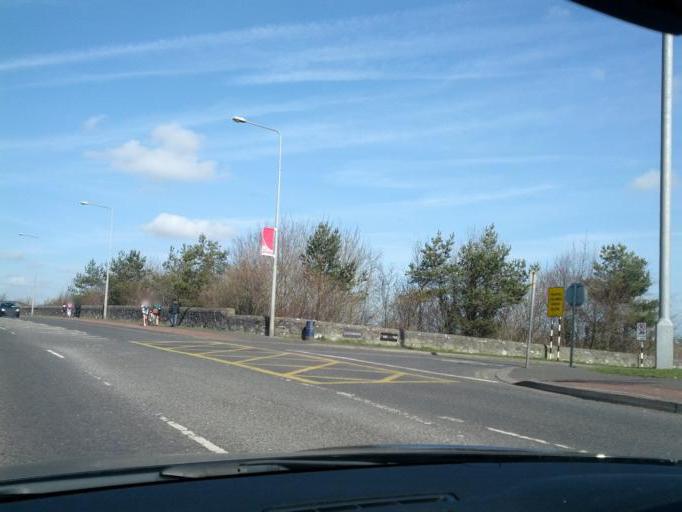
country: IE
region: Leinster
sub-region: Kildare
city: Maynooth
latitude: 53.3776
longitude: -6.5876
